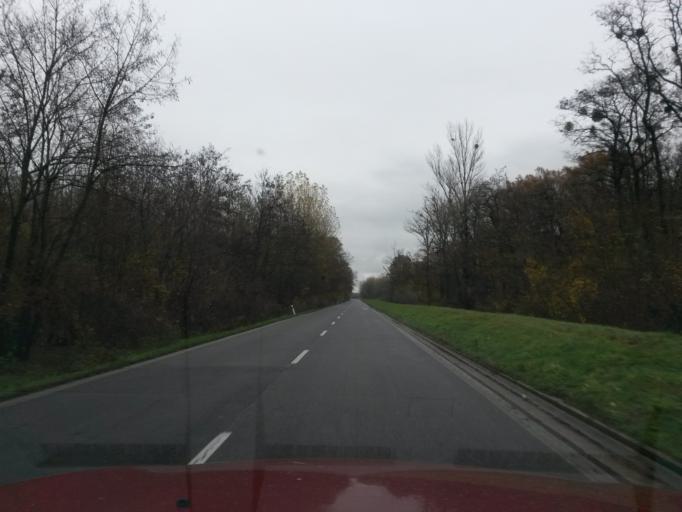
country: SK
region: Kosicky
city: Michalovce
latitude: 48.5694
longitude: 21.9488
